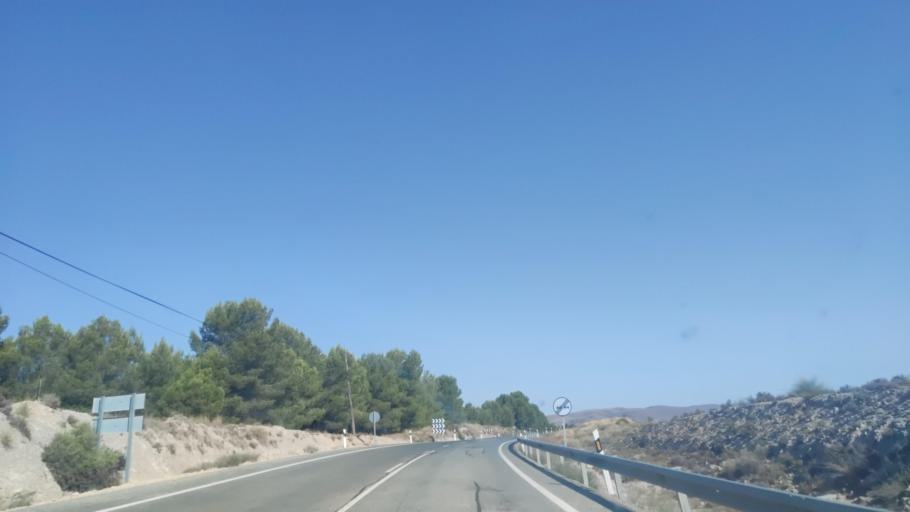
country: ES
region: Castille-La Mancha
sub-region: Provincia de Albacete
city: Hellin
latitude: 38.4835
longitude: -1.6167
